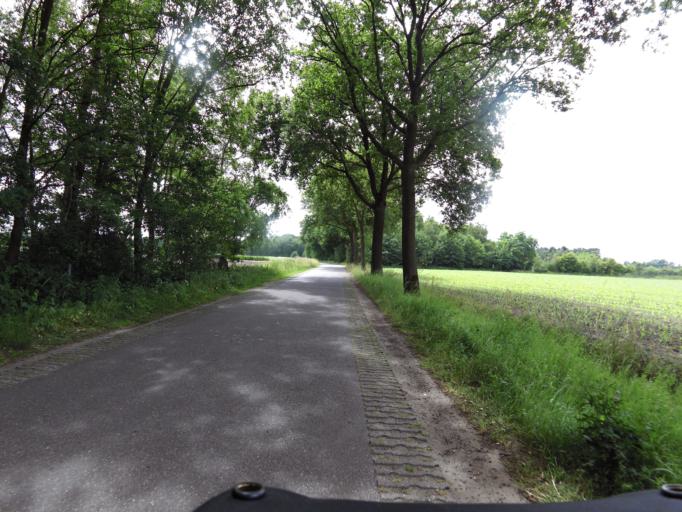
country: NL
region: North Brabant
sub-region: Gemeente Bladel en Netersel
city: Bladel
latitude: 51.3807
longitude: 5.1853
